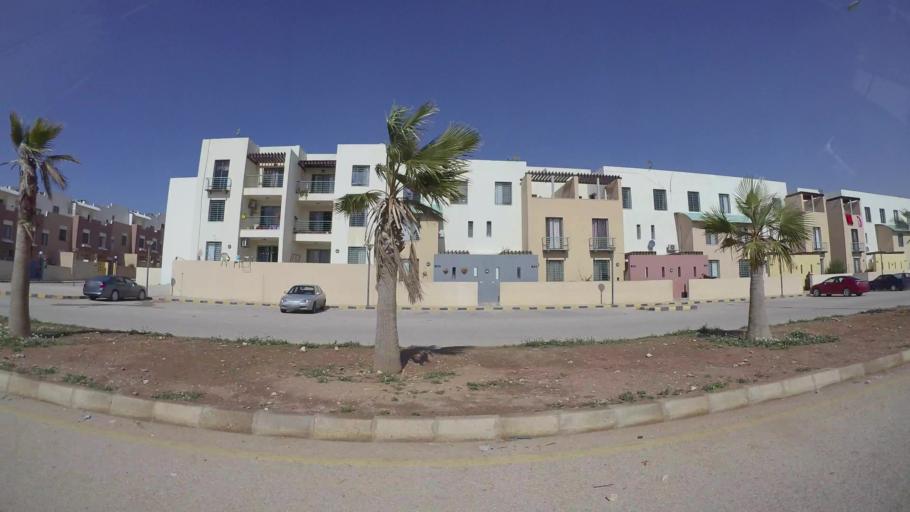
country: JO
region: Zarqa
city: Zarqa
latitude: 32.0706
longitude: 36.1108
